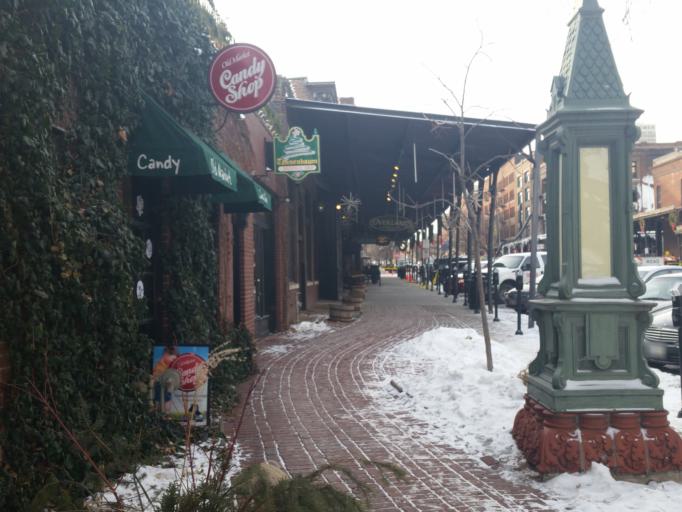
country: US
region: Nebraska
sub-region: Douglas County
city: Omaha
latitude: 41.2554
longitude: -95.9294
